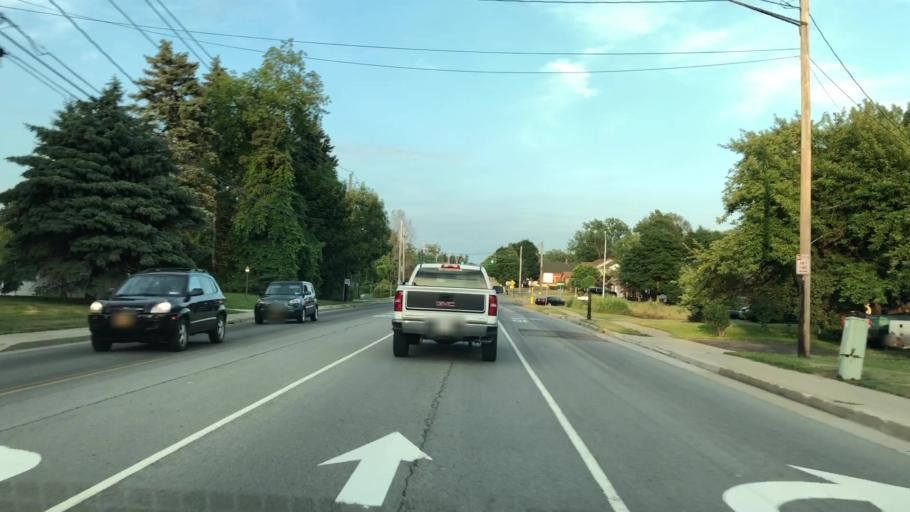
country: US
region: New York
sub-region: Erie County
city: Cheektowaga
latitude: 42.8814
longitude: -78.7319
